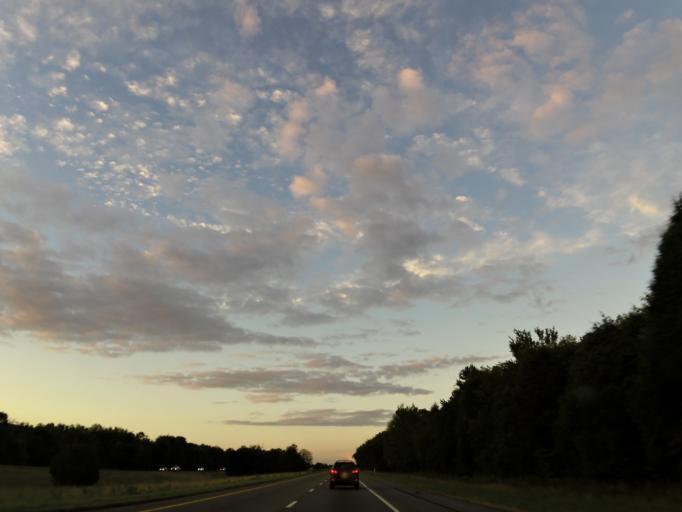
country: US
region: Tennessee
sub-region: Monroe County
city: Sweetwater
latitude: 35.6699
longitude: -84.4494
